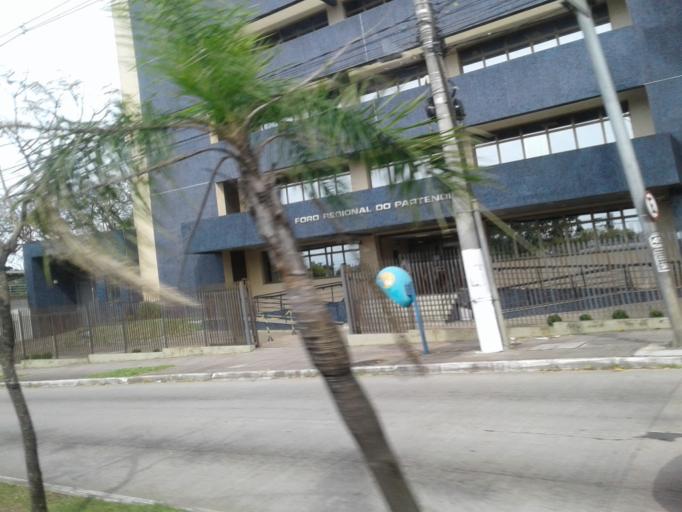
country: BR
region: Rio Grande do Sul
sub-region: Porto Alegre
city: Porto Alegre
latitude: -30.0715
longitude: -51.1902
